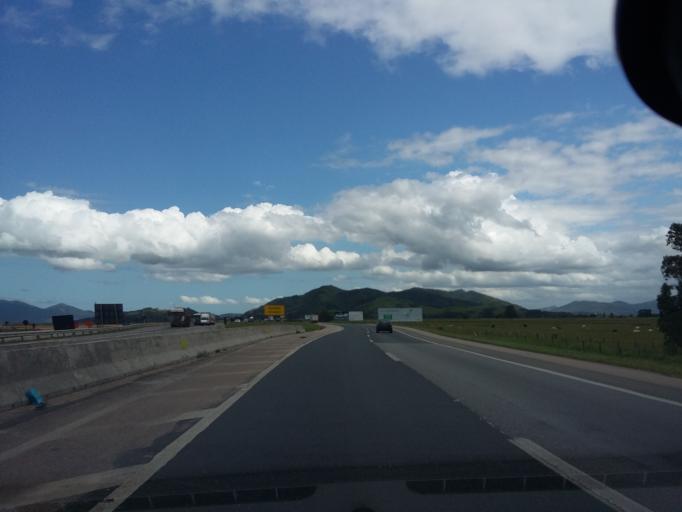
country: BR
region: Santa Catarina
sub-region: Tijucas
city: Tijucas
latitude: -27.2502
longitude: -48.6312
